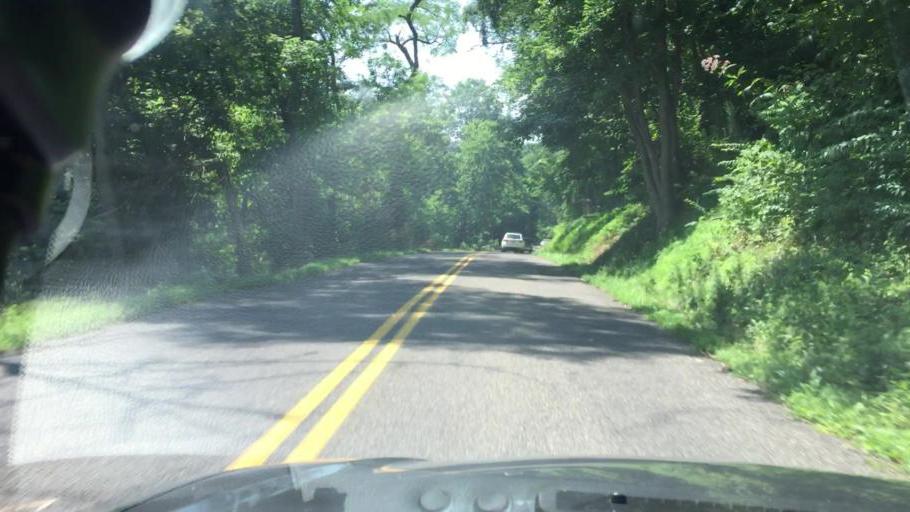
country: US
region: Pennsylvania
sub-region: Columbia County
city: Catawissa
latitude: 40.9563
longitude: -76.4467
